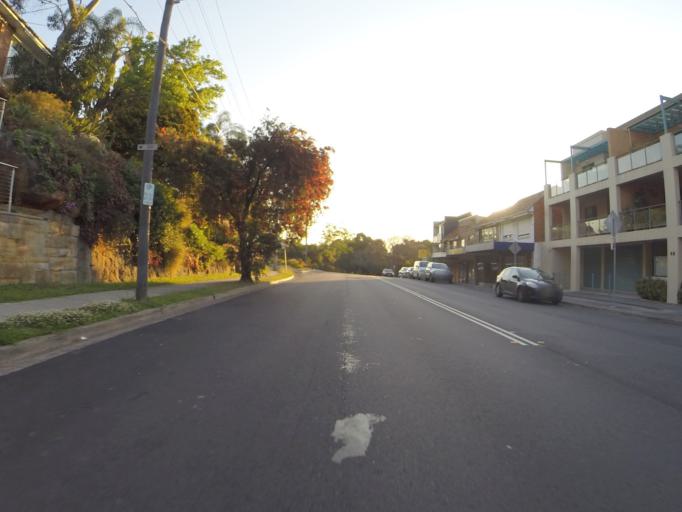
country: AU
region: New South Wales
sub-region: Rockdale
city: Bardwell Valley
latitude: -33.9321
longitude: 151.1255
